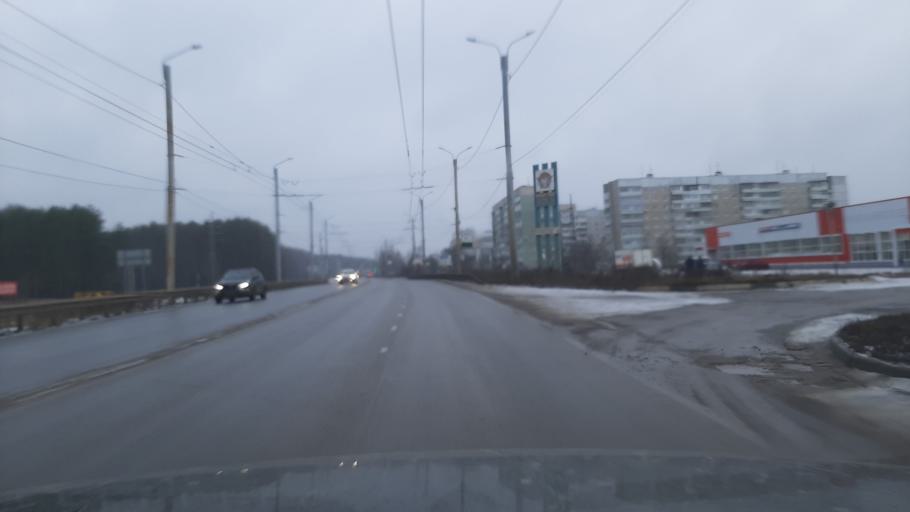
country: RU
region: Ivanovo
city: Kokhma
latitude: 56.9468
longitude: 41.0547
